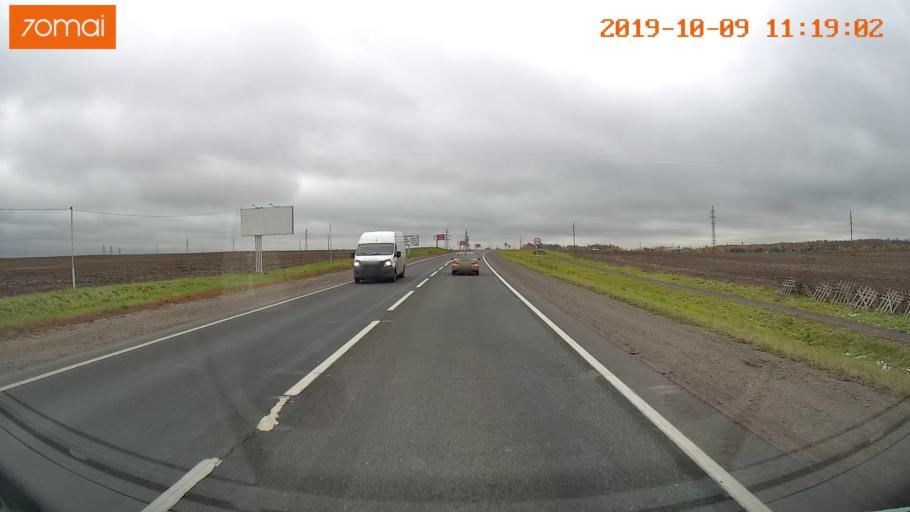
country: RU
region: Vologda
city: Vologda
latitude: 59.1629
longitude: 39.9231
